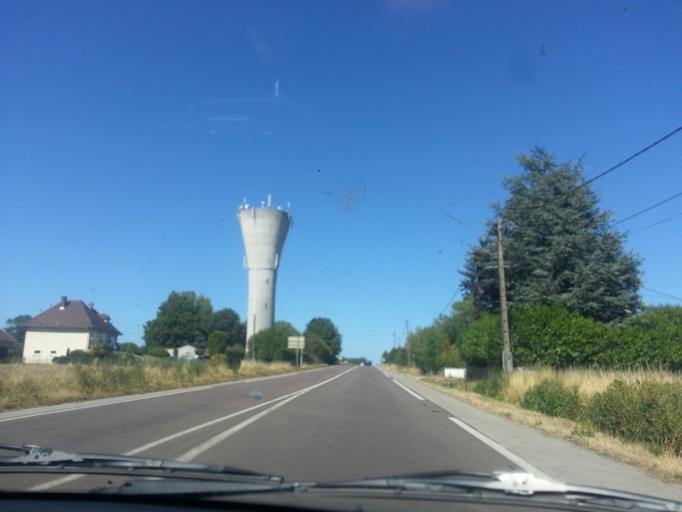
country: FR
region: Bourgogne
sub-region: Departement de Saone-et-Loire
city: Saint-Marcel
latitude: 46.7896
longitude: 4.9177
